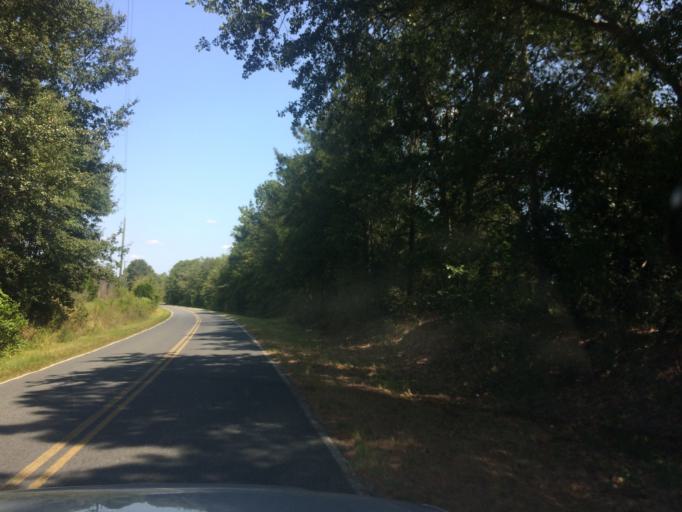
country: US
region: South Carolina
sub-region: Aiken County
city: Aiken
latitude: 33.5278
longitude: -81.6153
